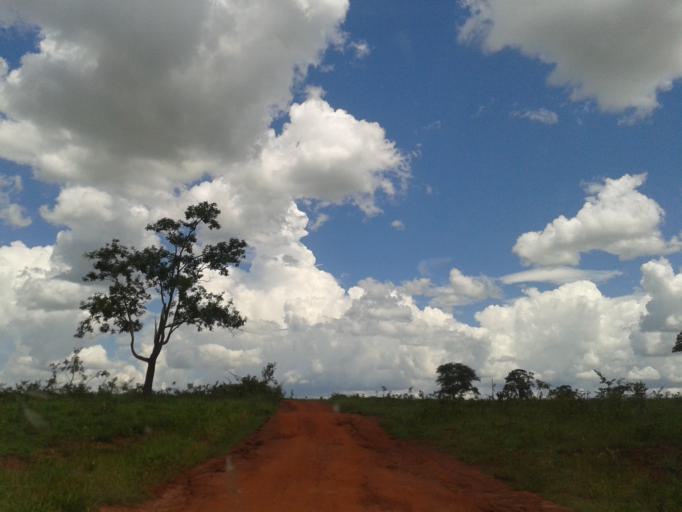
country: BR
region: Minas Gerais
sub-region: Capinopolis
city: Capinopolis
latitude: -18.7895
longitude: -49.8022
